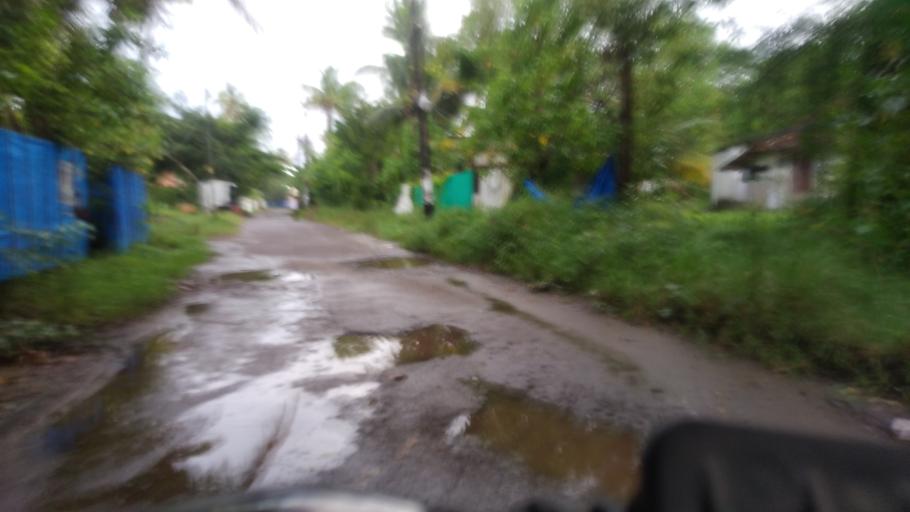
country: IN
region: Kerala
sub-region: Ernakulam
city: Cochin
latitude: 10.0119
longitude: 76.2175
